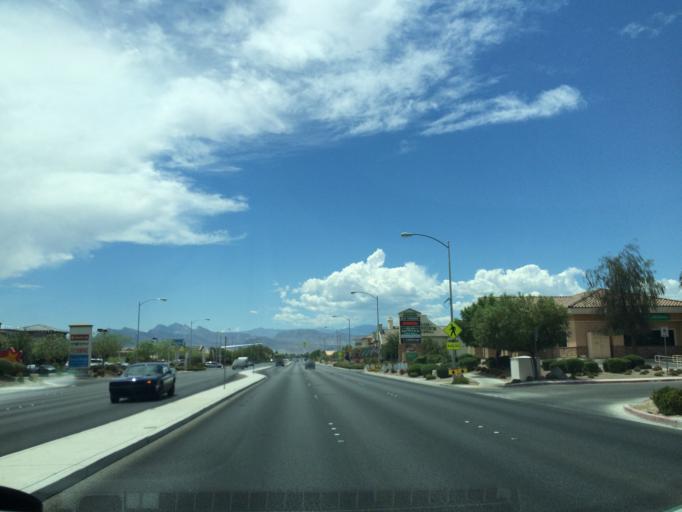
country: US
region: Nevada
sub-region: Clark County
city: North Las Vegas
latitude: 36.2616
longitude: -115.1826
